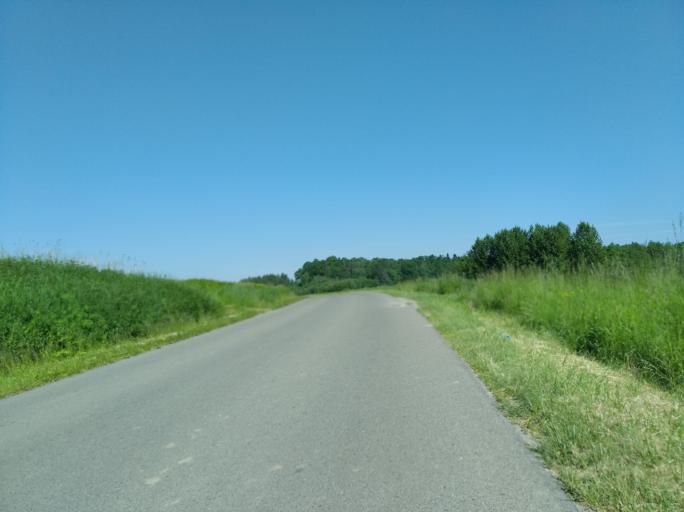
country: PL
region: Subcarpathian Voivodeship
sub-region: Powiat ropczycko-sedziszowski
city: Wielopole Skrzynskie
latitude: 49.9551
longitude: 21.6164
